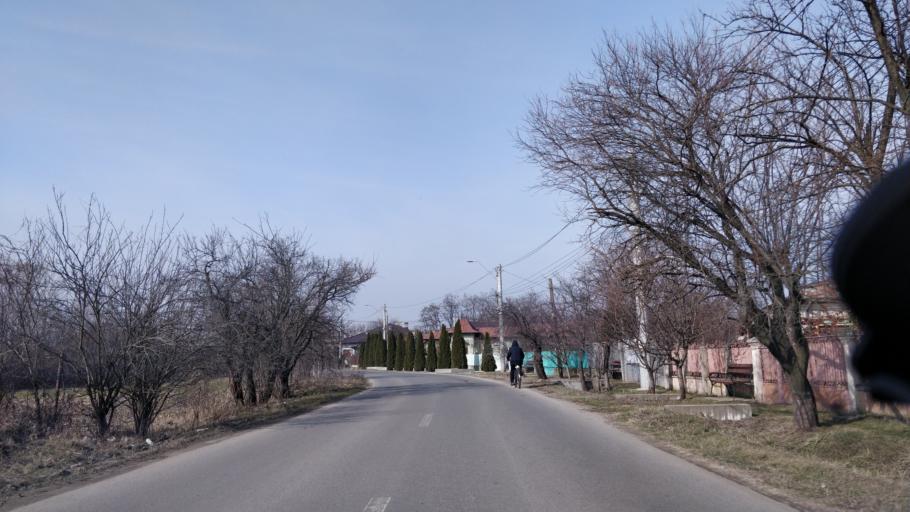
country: RO
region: Giurgiu
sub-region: Comuna Ulmi
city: Ulmi
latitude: 44.4673
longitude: 25.7716
